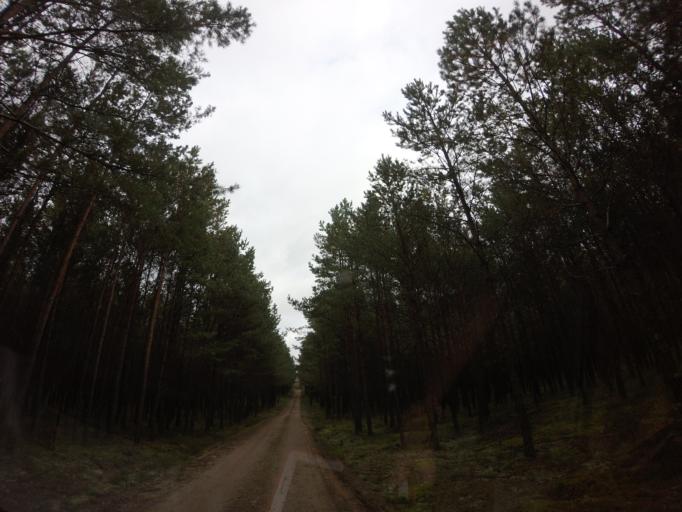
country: PL
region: West Pomeranian Voivodeship
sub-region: Powiat choszczenski
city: Drawno
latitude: 53.1788
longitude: 15.7590
